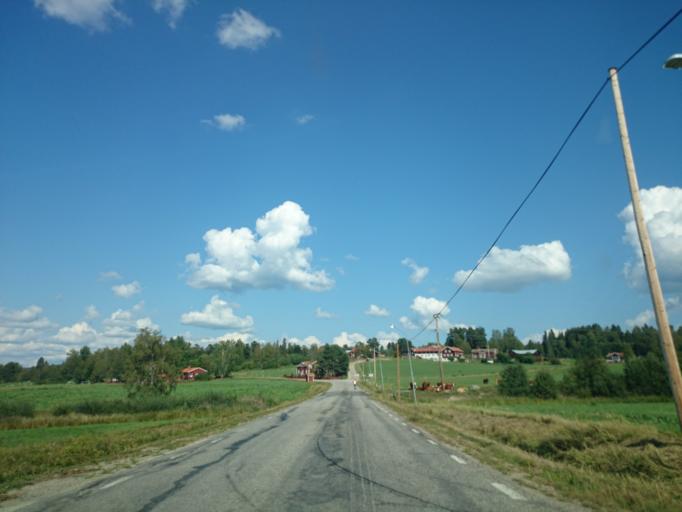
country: SE
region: Gaevleborg
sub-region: Ljusdals Kommun
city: Jaervsoe
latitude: 61.7123
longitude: 16.1978
